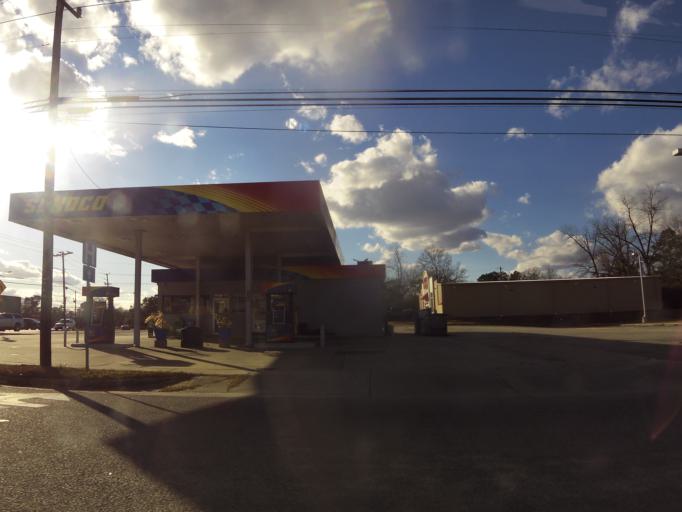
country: US
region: South Carolina
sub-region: Clarendon County
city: Manning
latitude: 33.6915
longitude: -80.2121
